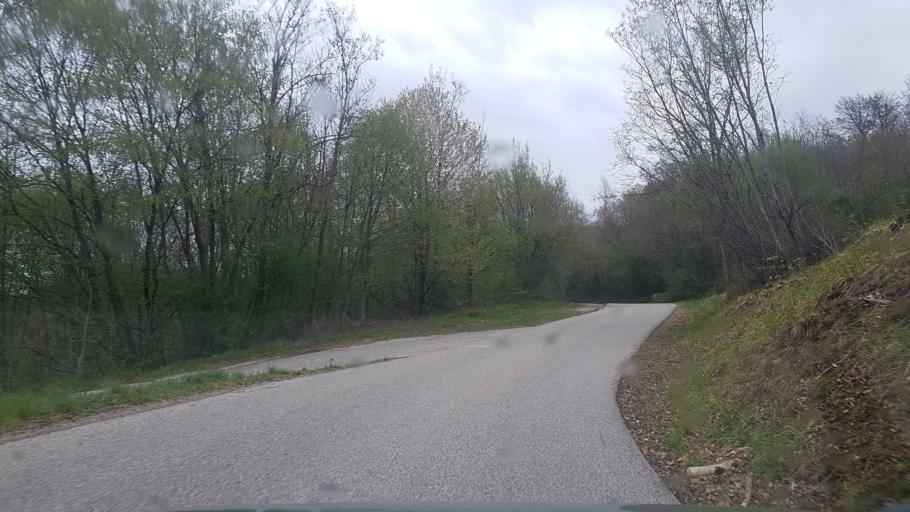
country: SI
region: Kanal
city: Deskle
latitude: 46.0270
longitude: 13.5748
